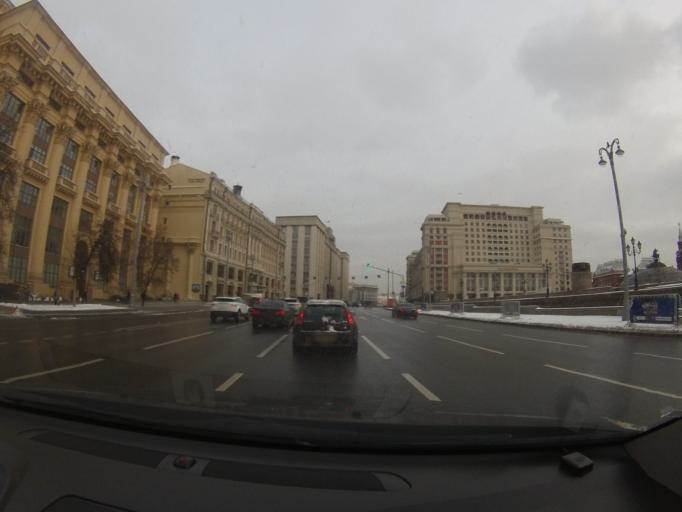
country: RU
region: Moskovskaya
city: Annino
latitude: 55.5988
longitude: 37.2536
